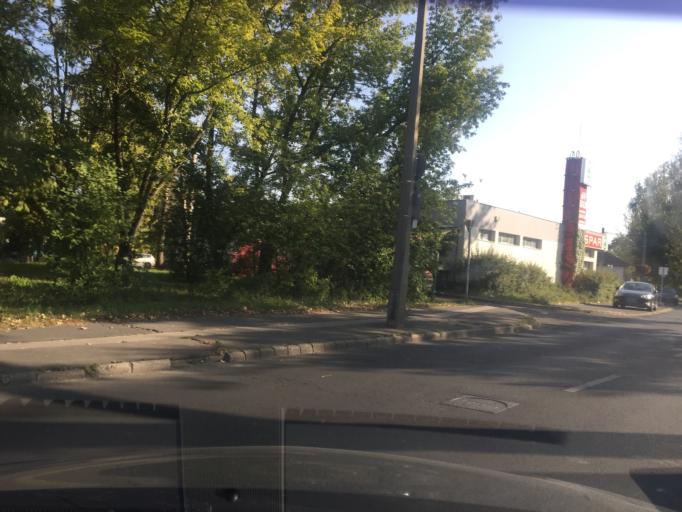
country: HU
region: Budapest
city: Budapest XV. keruelet
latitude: 47.5745
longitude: 19.1035
